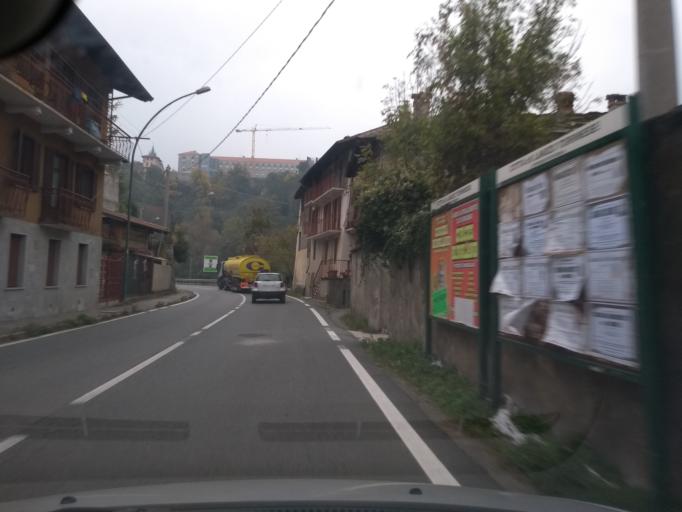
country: IT
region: Piedmont
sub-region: Provincia di Torino
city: Germagnano
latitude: 45.2683
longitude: 7.4765
